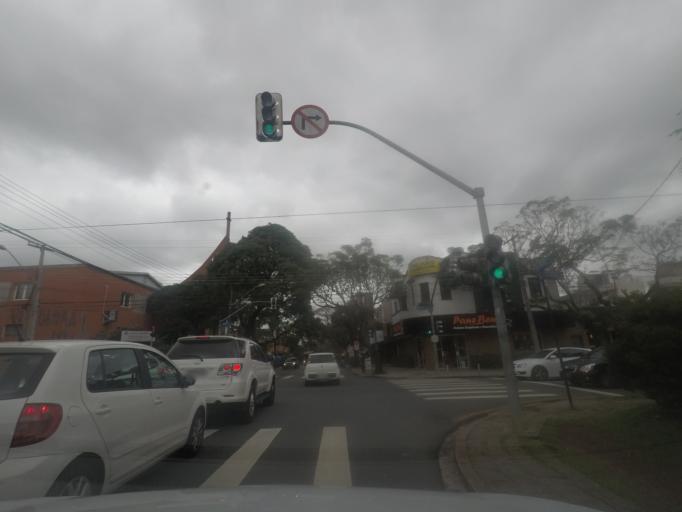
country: BR
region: Parana
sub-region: Curitiba
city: Curitiba
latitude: -25.4311
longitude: -49.2494
